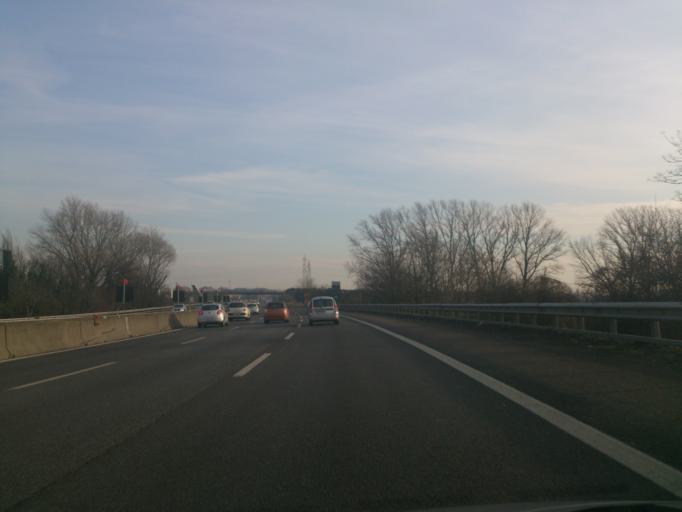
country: IT
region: Lombardy
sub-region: Citta metropolitana di Milano
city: Chiaravalle
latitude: 45.4179
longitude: 9.2474
